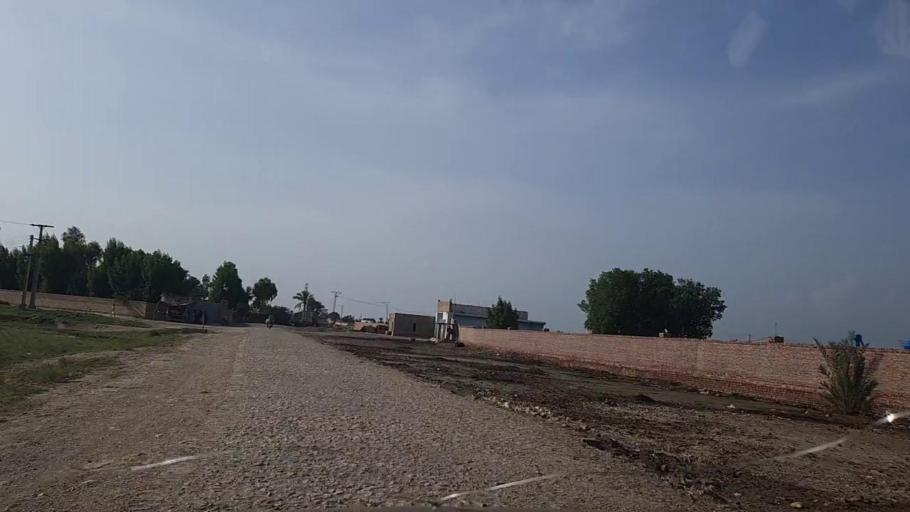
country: PK
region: Sindh
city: Ghotki
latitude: 28.0093
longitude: 69.2956
